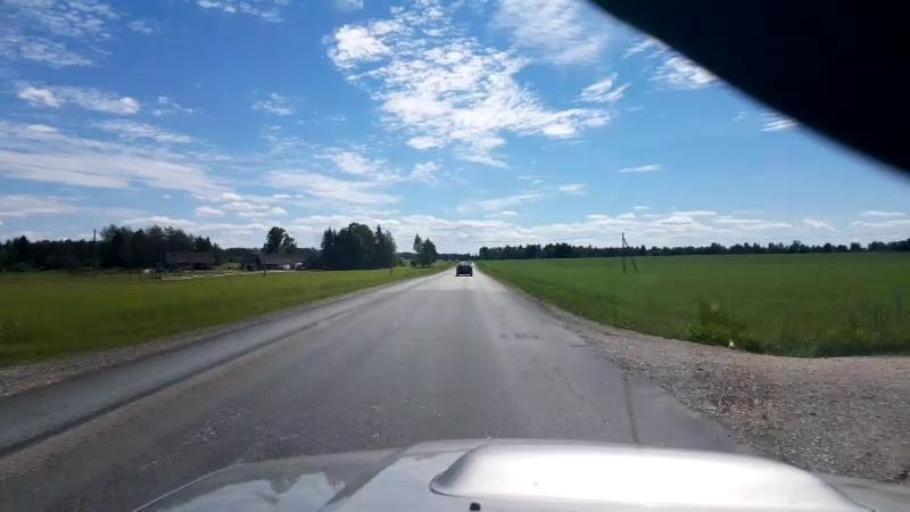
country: EE
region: Jogevamaa
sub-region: Jogeva linn
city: Jogeva
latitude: 58.8349
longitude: 26.2888
